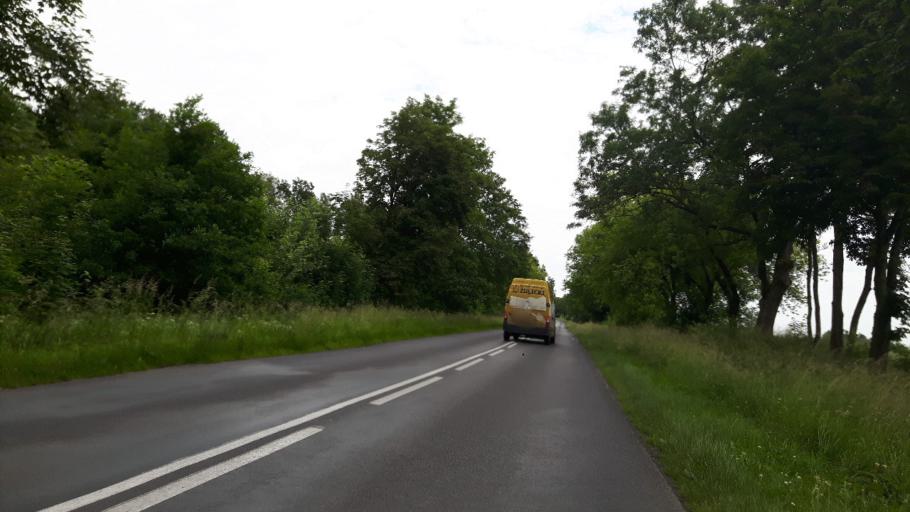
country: PL
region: West Pomeranian Voivodeship
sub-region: Powiat gryficki
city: Gryfice
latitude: 53.9467
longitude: 15.2236
